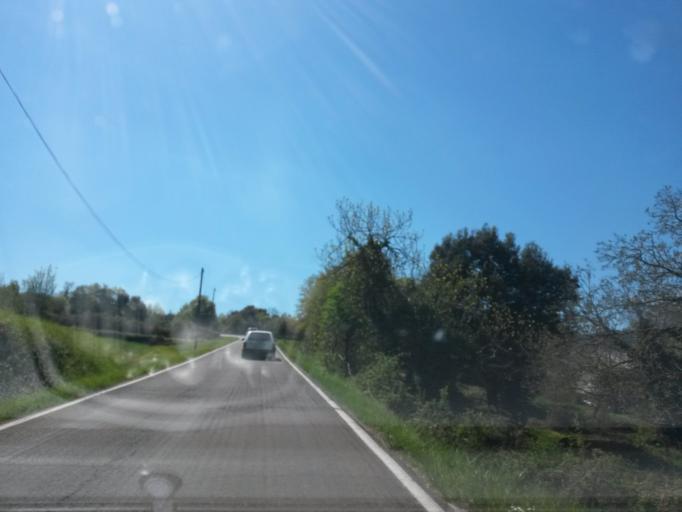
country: ES
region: Catalonia
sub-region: Provincia de Girona
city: Sant Cristofol de les Fonts
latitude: 42.1735
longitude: 2.5087
